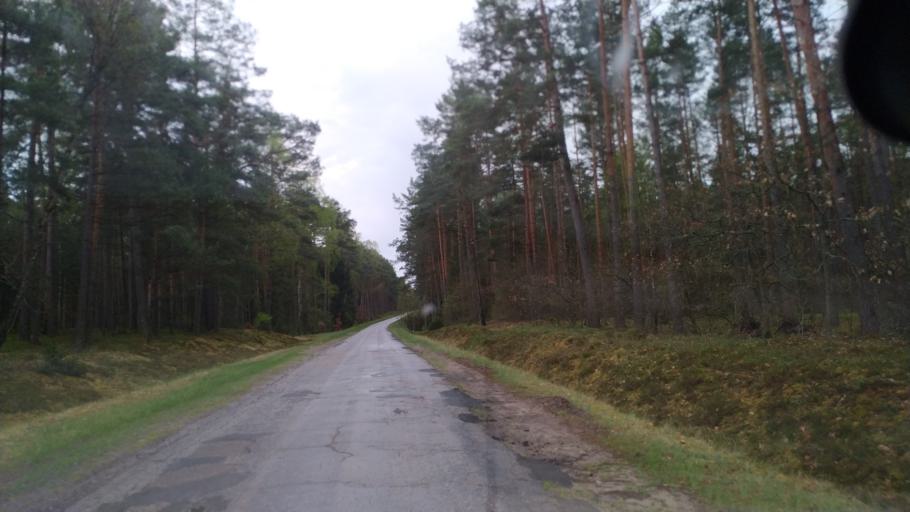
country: PL
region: Pomeranian Voivodeship
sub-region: Powiat starogardzki
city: Osiek
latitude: 53.6725
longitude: 18.4771
